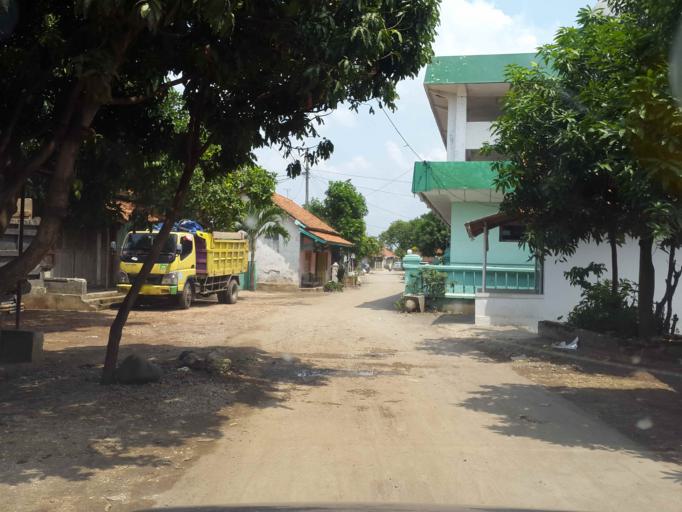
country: ID
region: Central Java
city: Margasari
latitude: -7.0672
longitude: 109.0366
